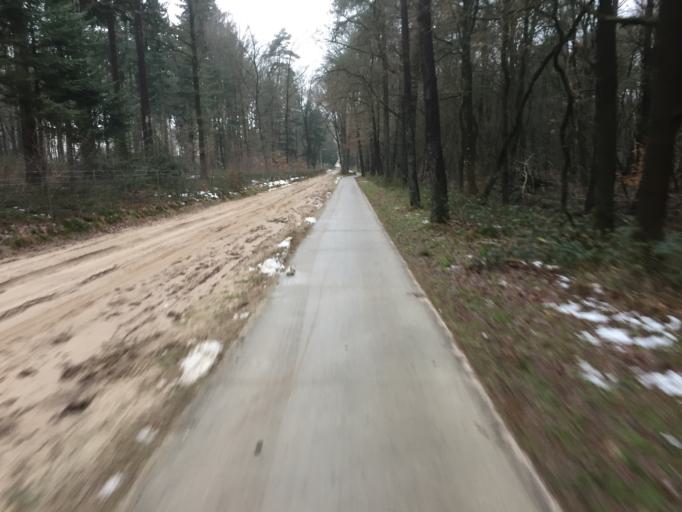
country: NL
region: Gelderland
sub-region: Gemeente Ede
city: Bennekom
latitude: 52.0235
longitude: 5.6909
